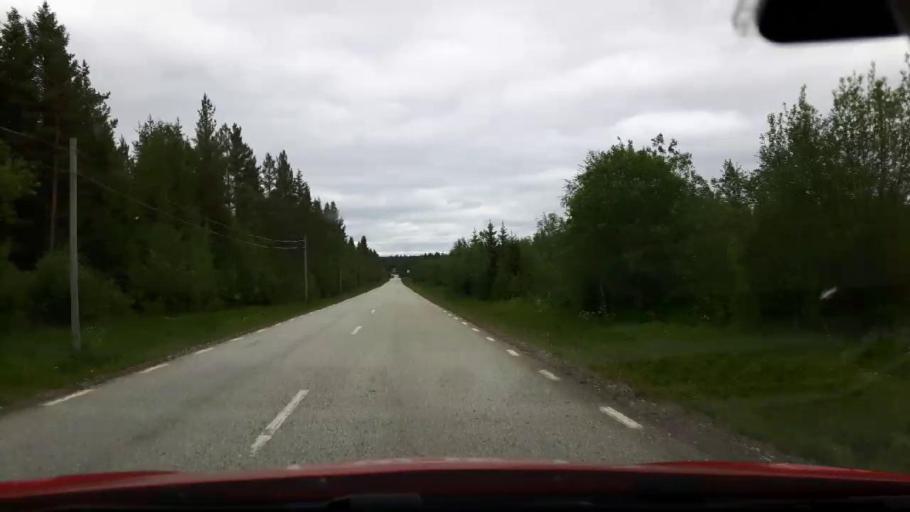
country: SE
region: Jaemtland
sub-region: Stroemsunds Kommun
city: Stroemsund
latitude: 63.3330
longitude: 15.7636
